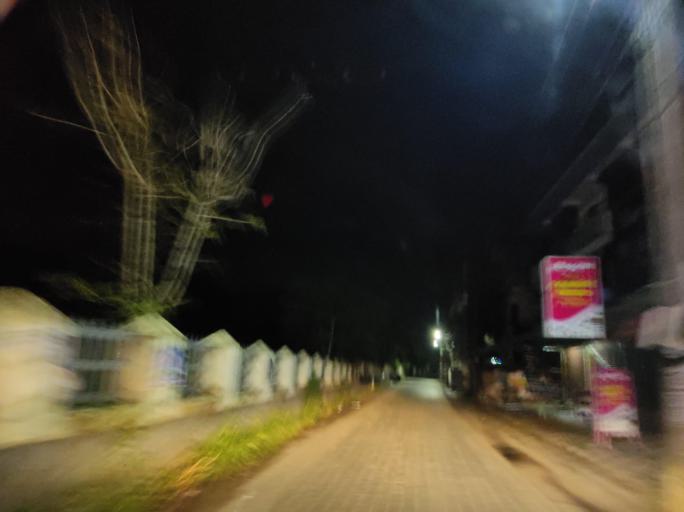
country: IN
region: Kerala
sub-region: Alappuzha
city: Shertallai
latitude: 9.6847
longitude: 76.3412
